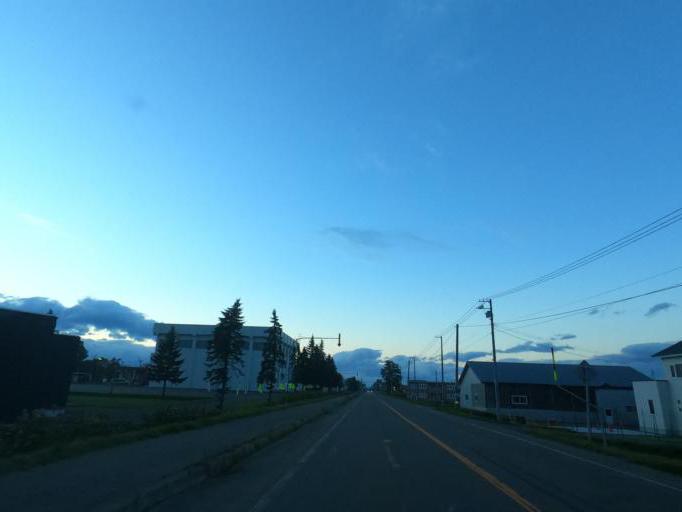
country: JP
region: Hokkaido
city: Obihiro
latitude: 42.6500
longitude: 143.1934
